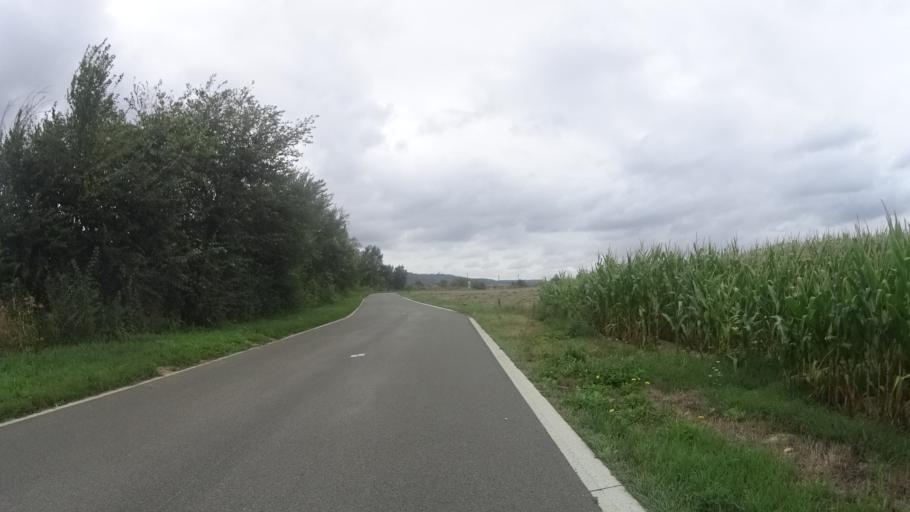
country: FR
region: Picardie
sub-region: Departement de l'Oise
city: Dreslincourt
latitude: 49.5099
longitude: 2.9440
